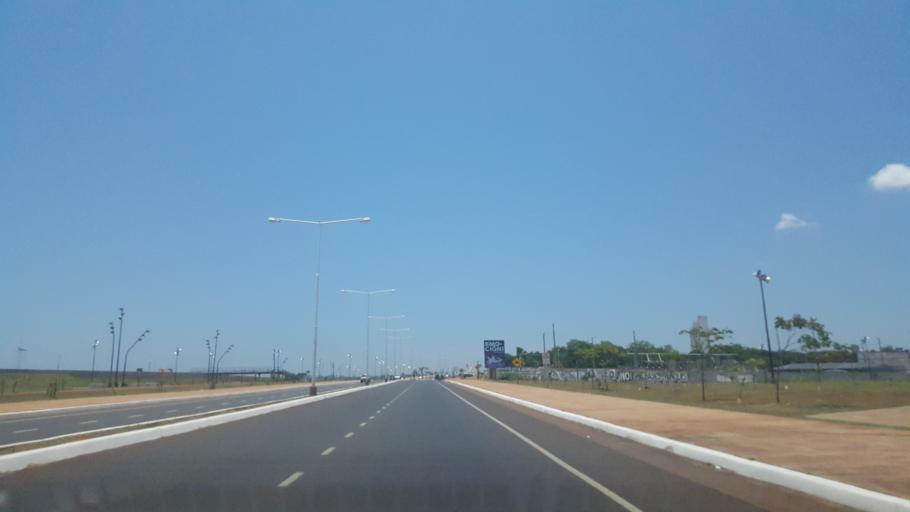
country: AR
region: Misiones
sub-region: Departamento de Capital
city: Posadas
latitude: -27.3767
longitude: -55.8858
